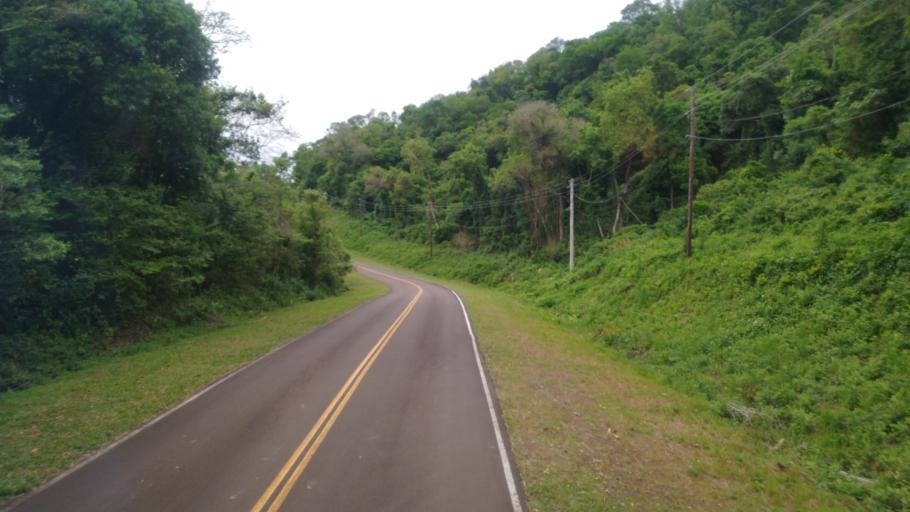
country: AR
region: Misiones
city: Cerro Cora
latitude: -27.4476
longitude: -55.5681
